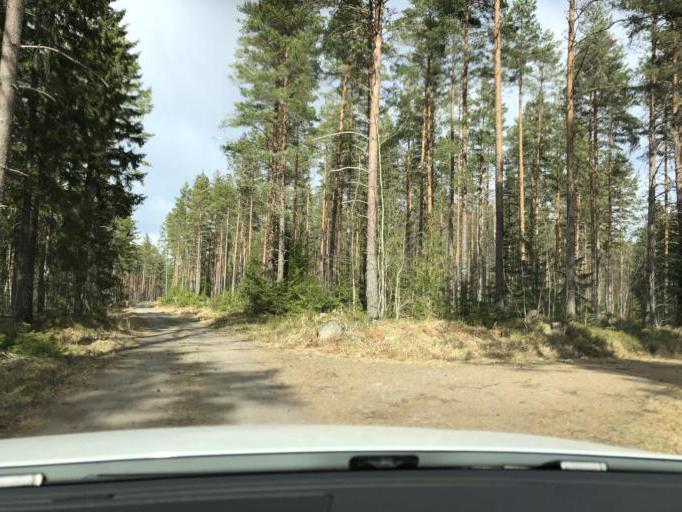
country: SE
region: Gaevleborg
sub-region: Gavle Kommun
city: Hedesunda
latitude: 60.3275
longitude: 17.1063
